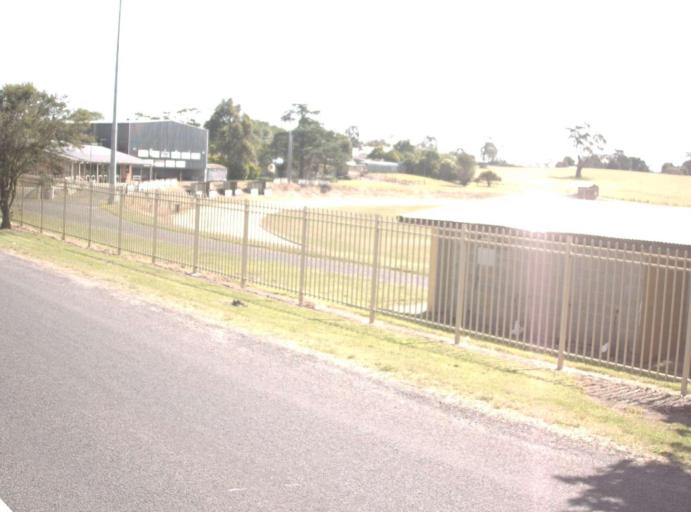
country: AU
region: Victoria
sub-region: Baw Baw
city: Warragul
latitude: -38.3408
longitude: 145.7650
